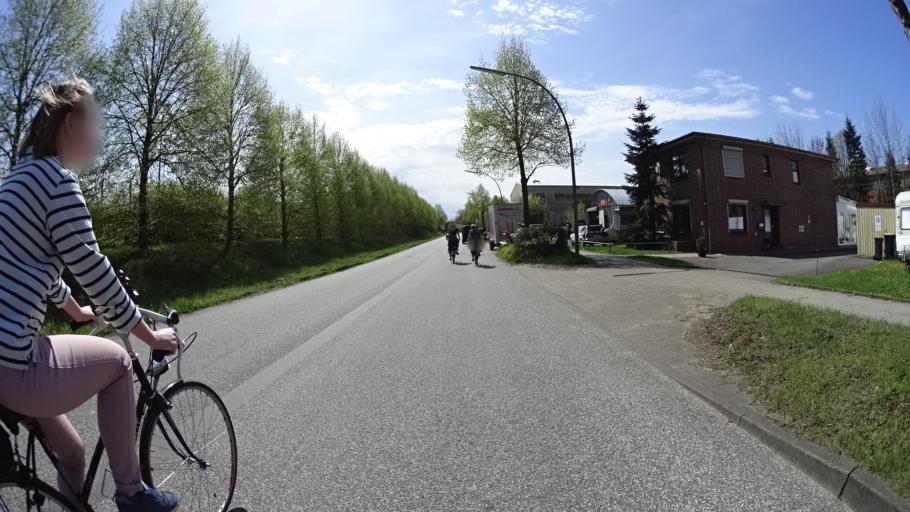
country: DE
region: Hamburg
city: Altona
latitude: 53.5375
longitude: 9.8586
